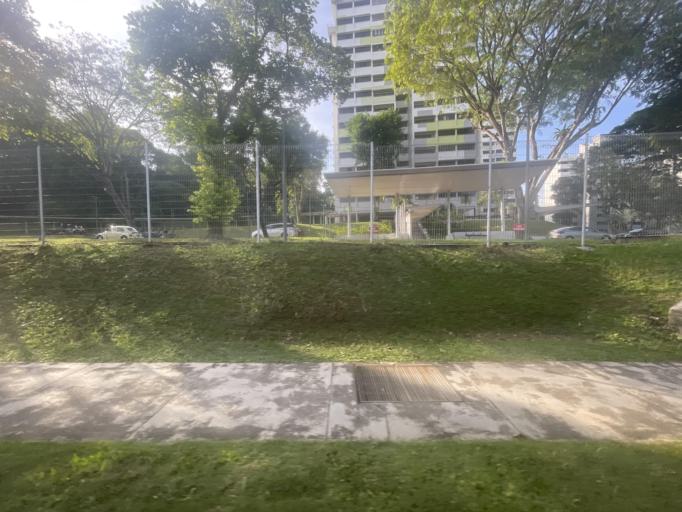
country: SG
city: Singapore
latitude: 1.3121
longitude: 103.7737
